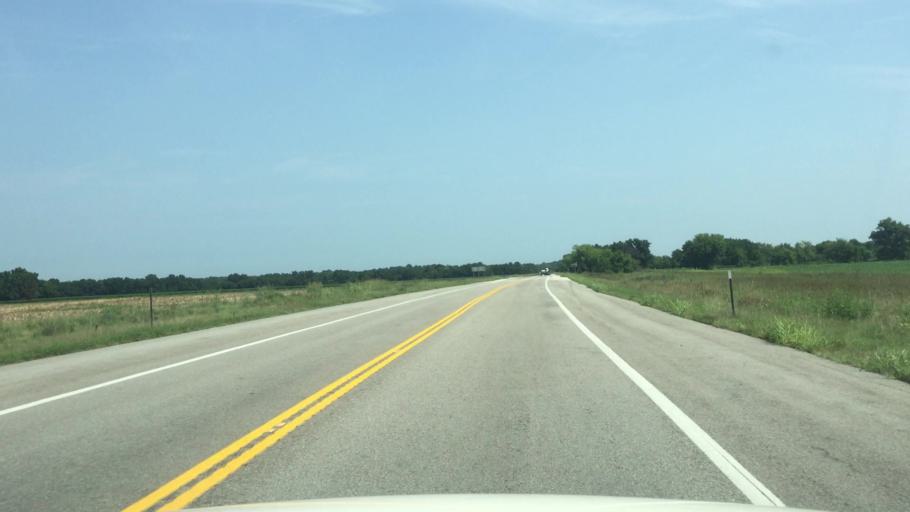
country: US
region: Kansas
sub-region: Montgomery County
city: Coffeyville
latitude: 37.1198
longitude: -95.5825
